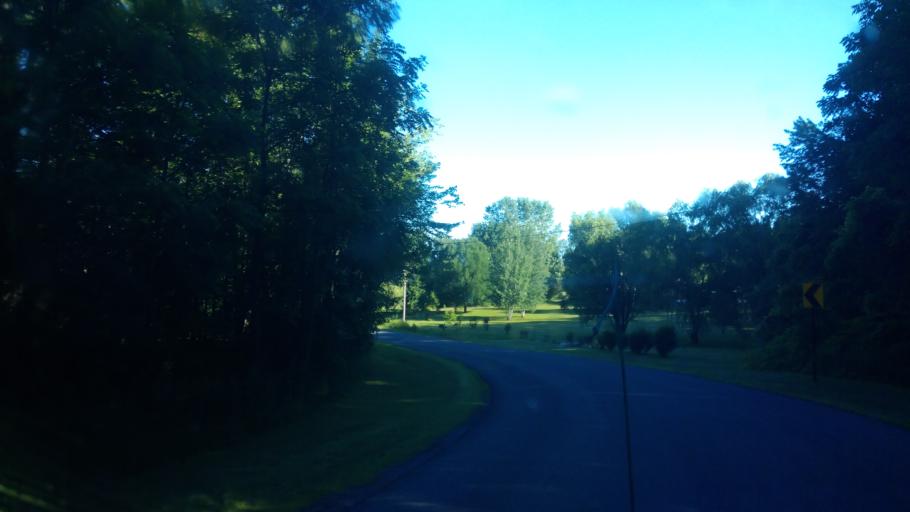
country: US
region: New York
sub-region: Wayne County
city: Lyons
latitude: 43.1349
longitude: -77.0380
